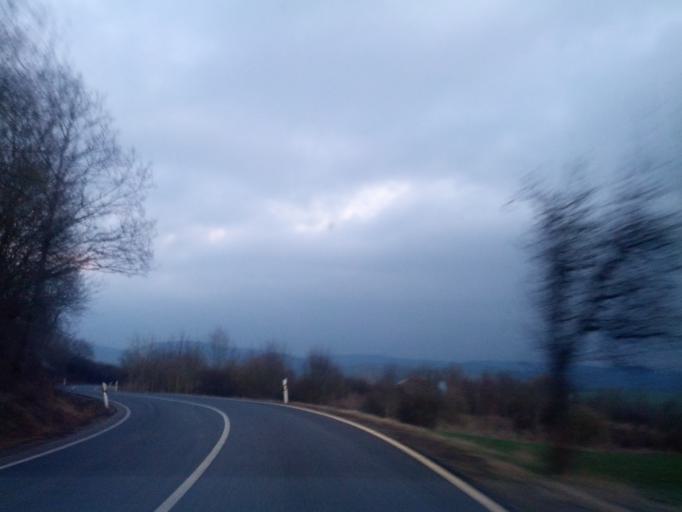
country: DE
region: Thuringia
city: Ifta
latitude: 51.0564
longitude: 10.2072
